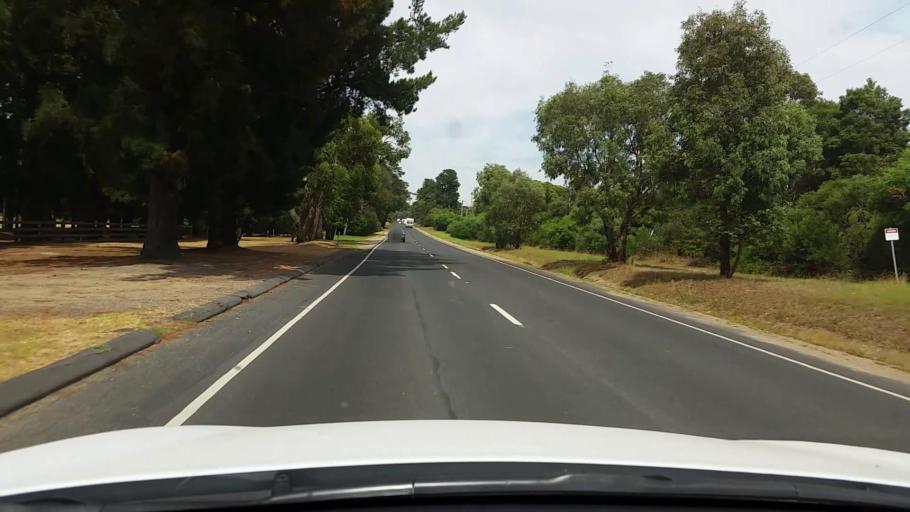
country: AU
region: Victoria
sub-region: Mornington Peninsula
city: Balnarring
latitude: -38.3684
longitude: 145.1346
